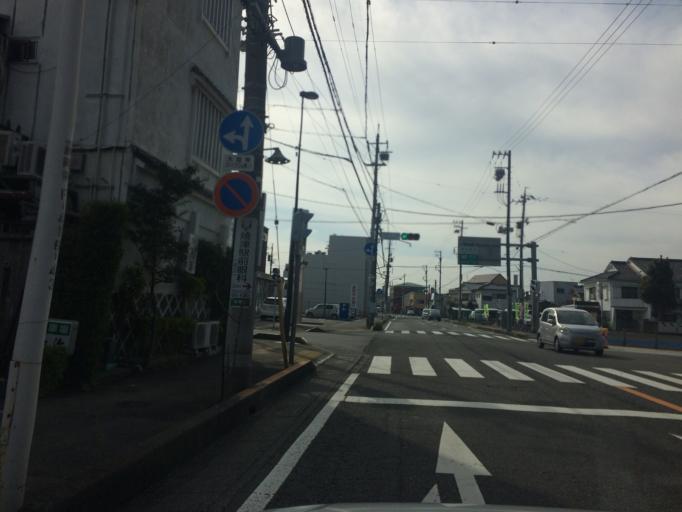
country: JP
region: Shizuoka
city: Yaizu
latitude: 34.8691
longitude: 138.3217
